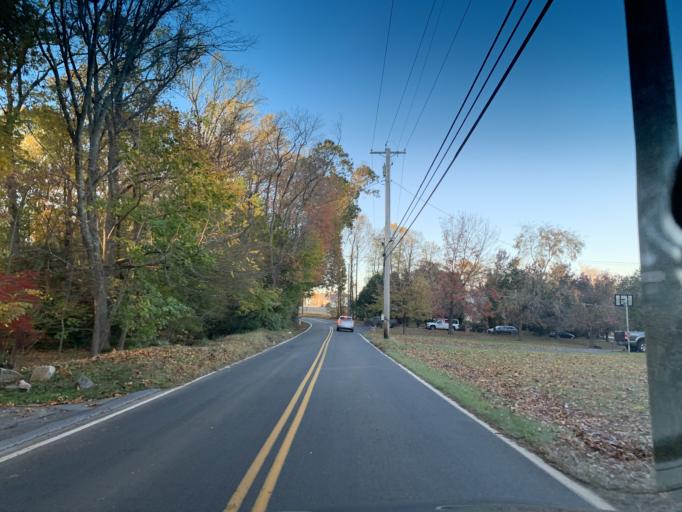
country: US
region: Maryland
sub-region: Harford County
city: Bel Air North
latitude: 39.5586
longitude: -76.3983
